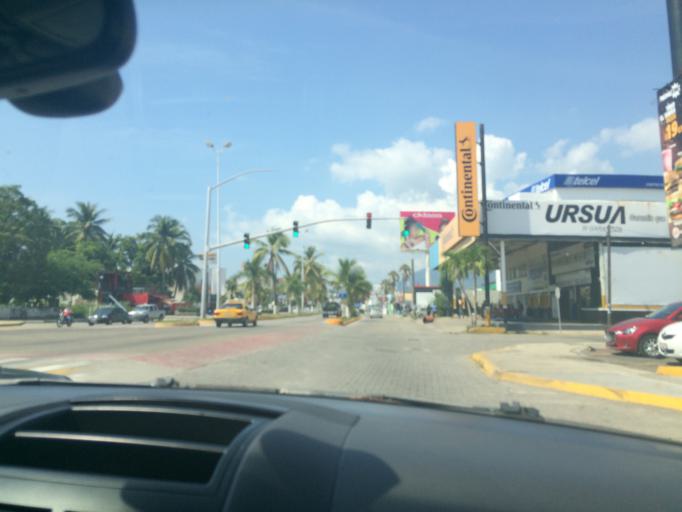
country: MX
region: Colima
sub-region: Manzanillo
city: Manzanillo
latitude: 19.1025
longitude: -104.3276
